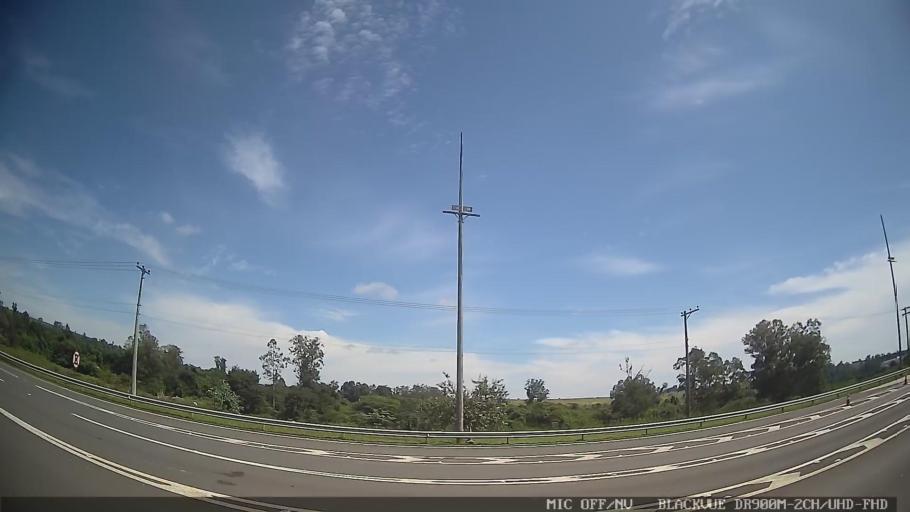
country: BR
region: Sao Paulo
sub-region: Porto Feliz
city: Porto Feliz
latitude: -23.2277
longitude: -47.5634
